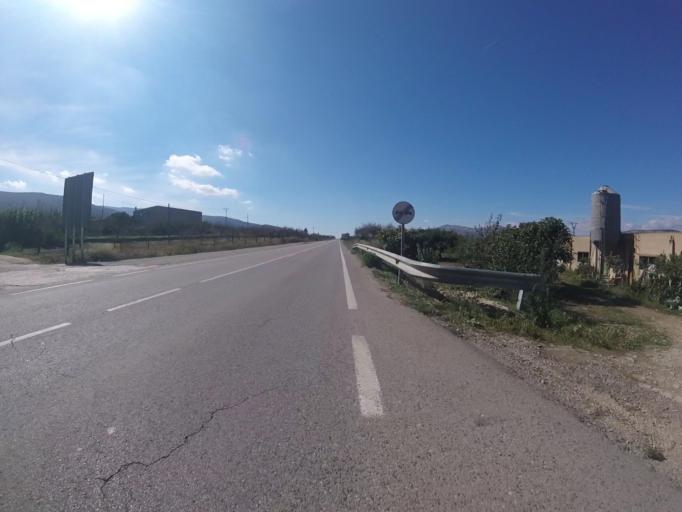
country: ES
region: Valencia
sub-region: Provincia de Castello
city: Albocasser
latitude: 40.3425
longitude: -0.0066
